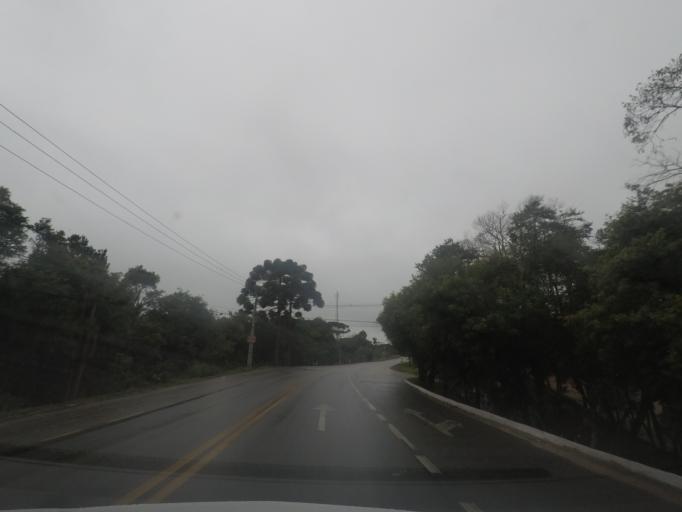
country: BR
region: Parana
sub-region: Colombo
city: Colombo
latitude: -25.3137
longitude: -49.1500
